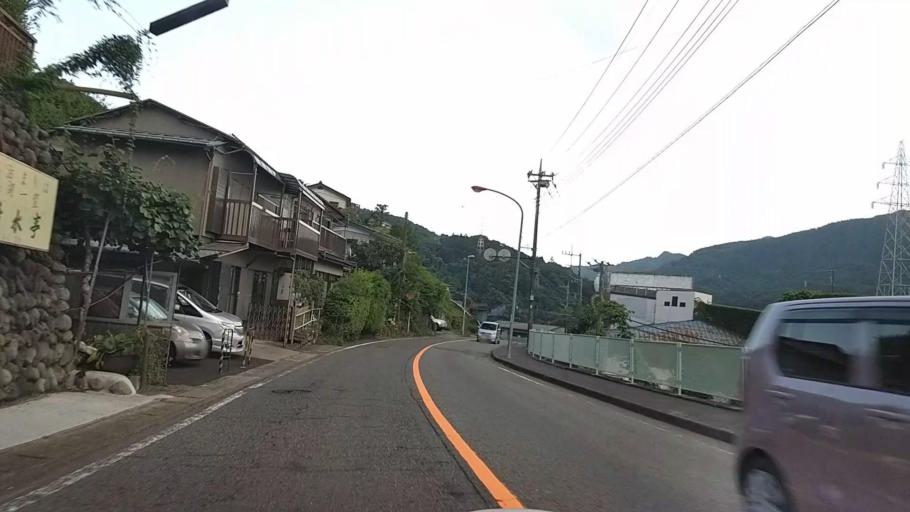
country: JP
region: Yamanashi
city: Uenohara
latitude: 35.6146
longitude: 139.1885
